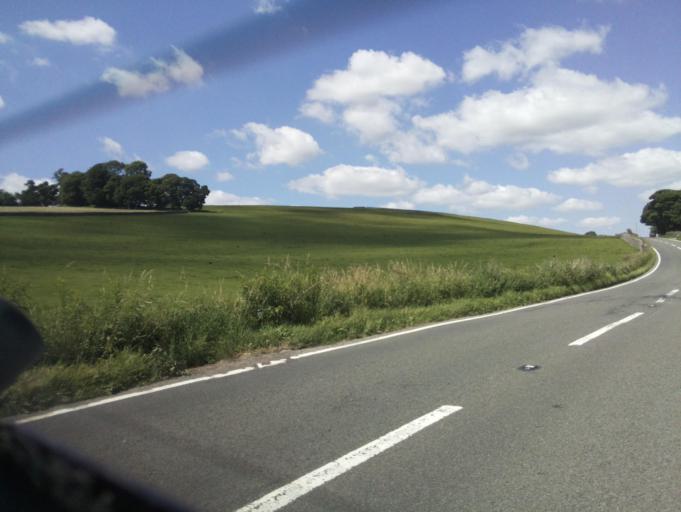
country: GB
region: England
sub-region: Derbyshire
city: Ashbourne
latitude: 53.0774
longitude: -1.7579
